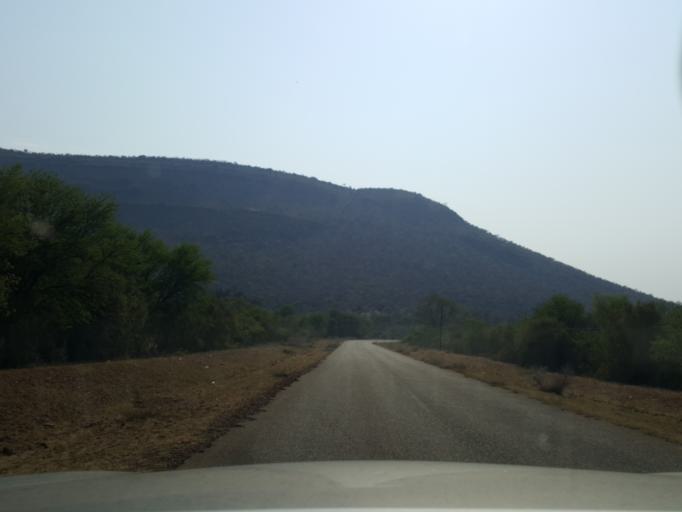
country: BW
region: South East
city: Lobatse
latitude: -25.3275
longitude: 25.7701
